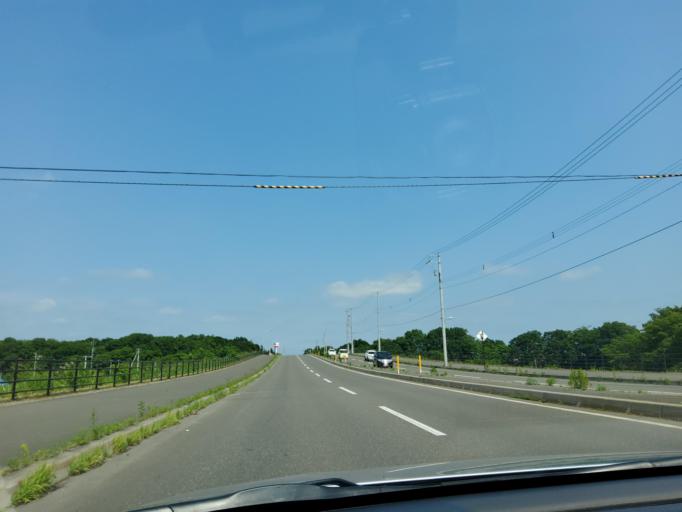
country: JP
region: Hokkaido
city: Obihiro
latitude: 42.9120
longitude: 143.0647
